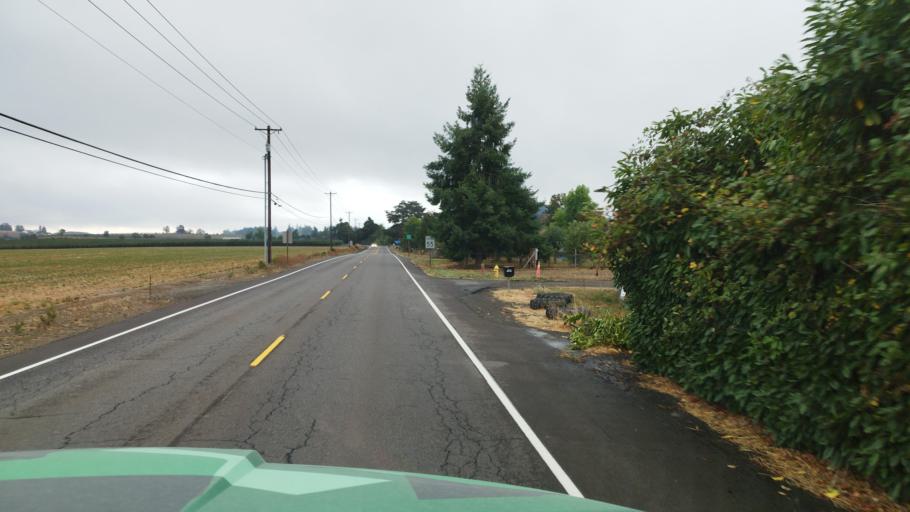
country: US
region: Oregon
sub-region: Yamhill County
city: Yamhill
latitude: 45.3346
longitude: -123.1856
